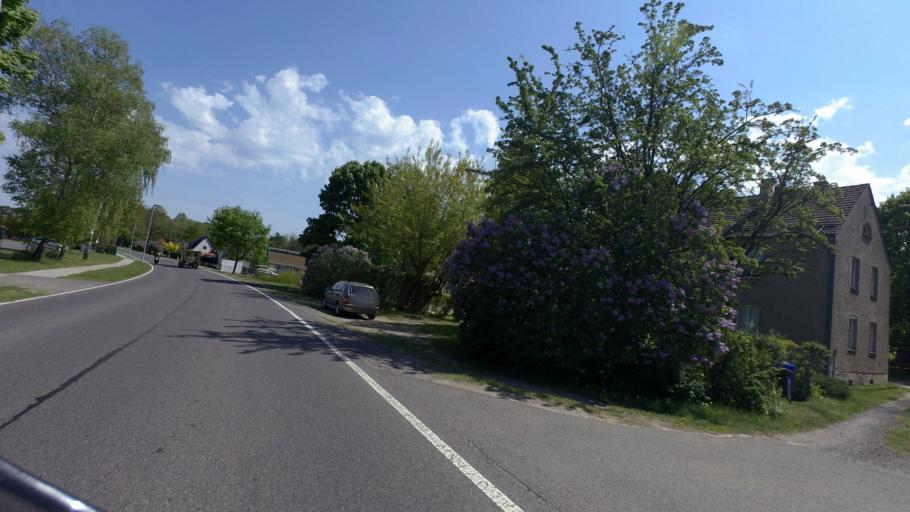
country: DE
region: Brandenburg
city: Lieberose
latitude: 51.9804
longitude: 14.2898
